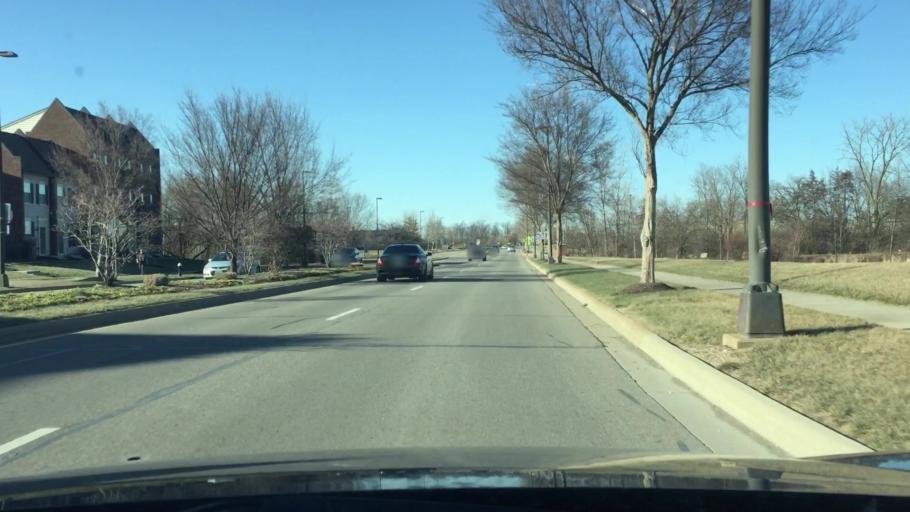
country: US
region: Ohio
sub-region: Franklin County
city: Hilliard
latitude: 40.0373
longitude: -83.1311
